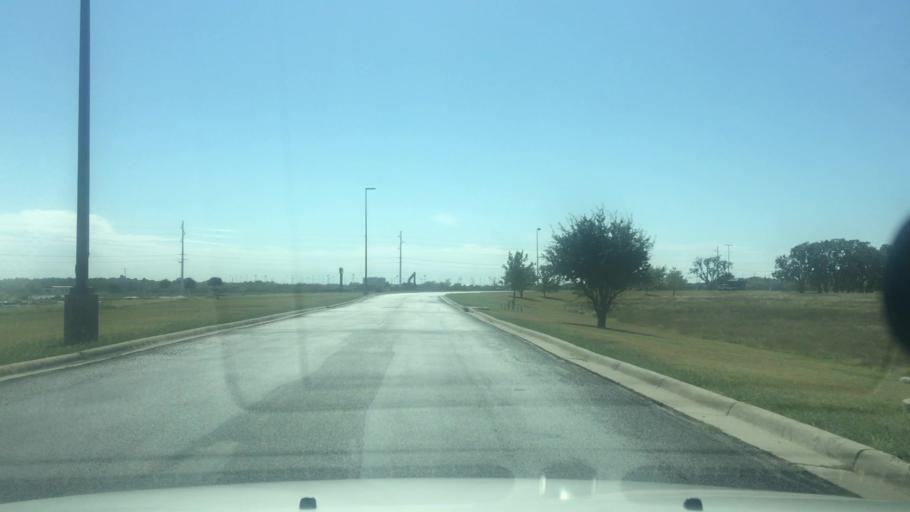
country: US
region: Texas
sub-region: Denton County
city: Denton
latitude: 33.2523
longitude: -97.1497
